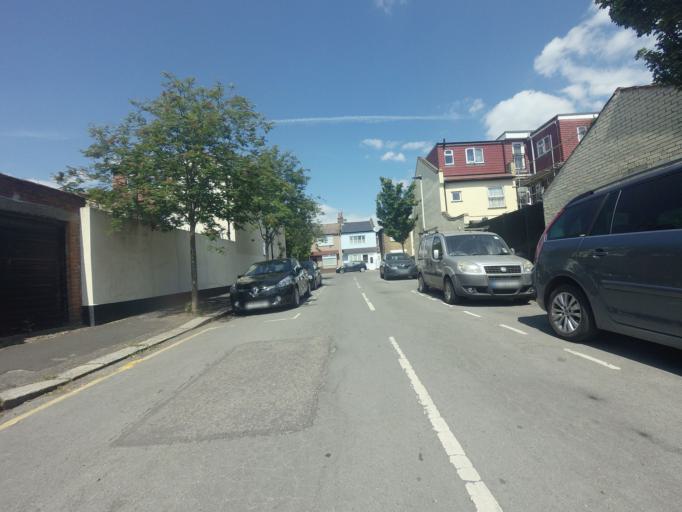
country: GB
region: England
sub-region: Greater London
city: East Ham
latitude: 51.5515
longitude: 0.0116
